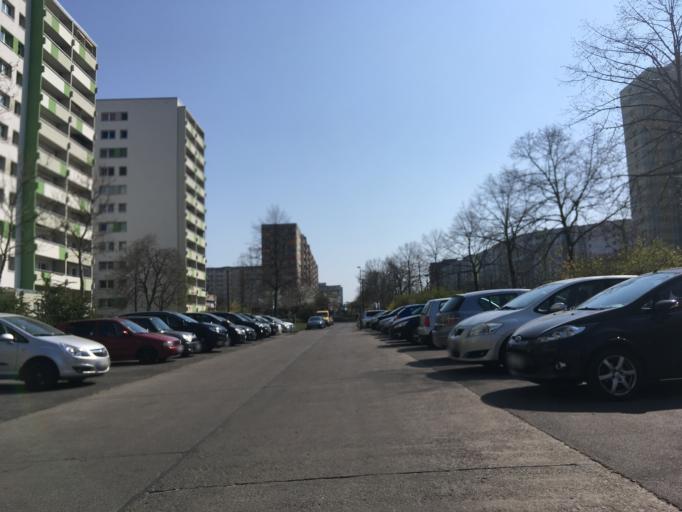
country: DE
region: Berlin
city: Neu-Hohenschoenhausen
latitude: 52.5672
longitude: 13.5010
